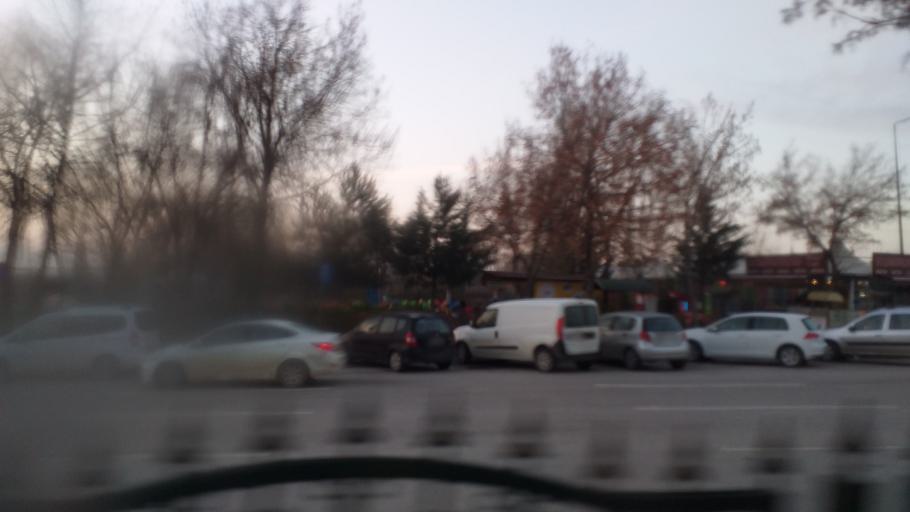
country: TR
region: Ankara
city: Ankara
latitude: 39.9689
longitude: 32.8194
